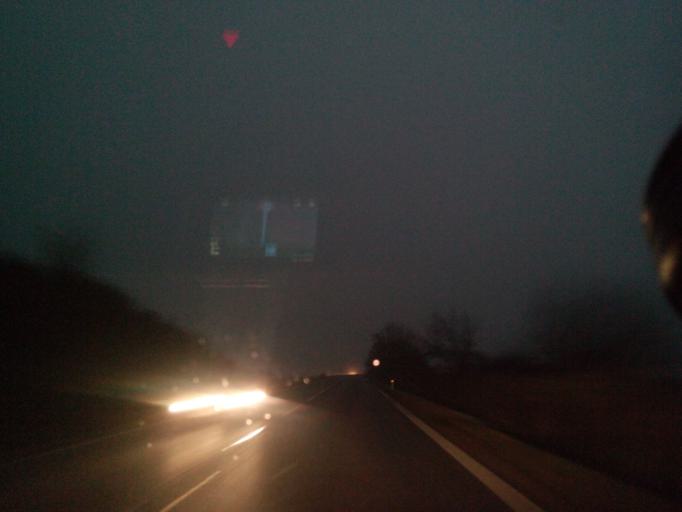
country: SK
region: Presovsky
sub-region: Okres Presov
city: Presov
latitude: 49.0060
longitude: 21.1623
